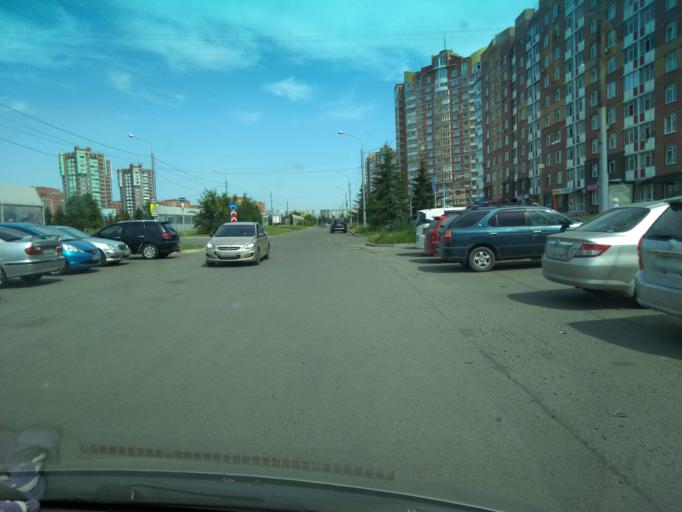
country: RU
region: Krasnoyarskiy
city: Krasnoyarsk
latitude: 56.0513
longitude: 92.9135
